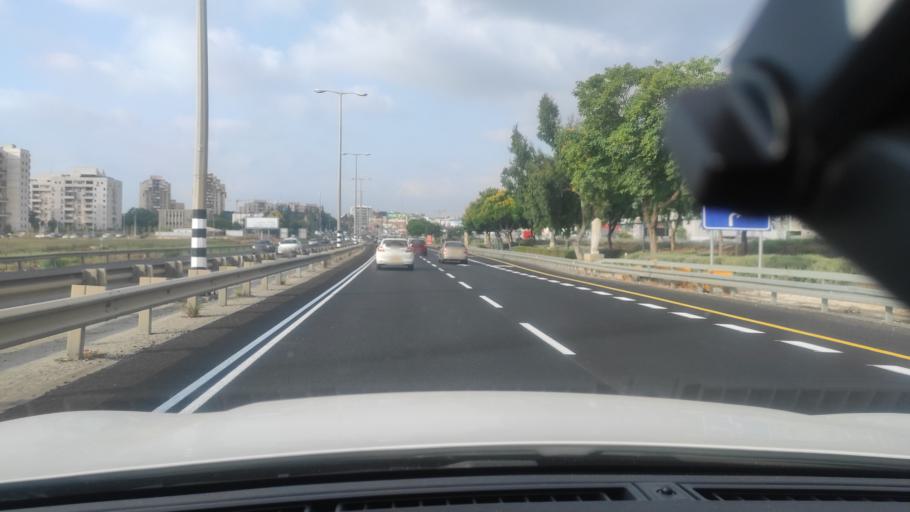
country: IL
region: Central District
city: Petah Tiqwa
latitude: 32.1060
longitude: 34.8998
